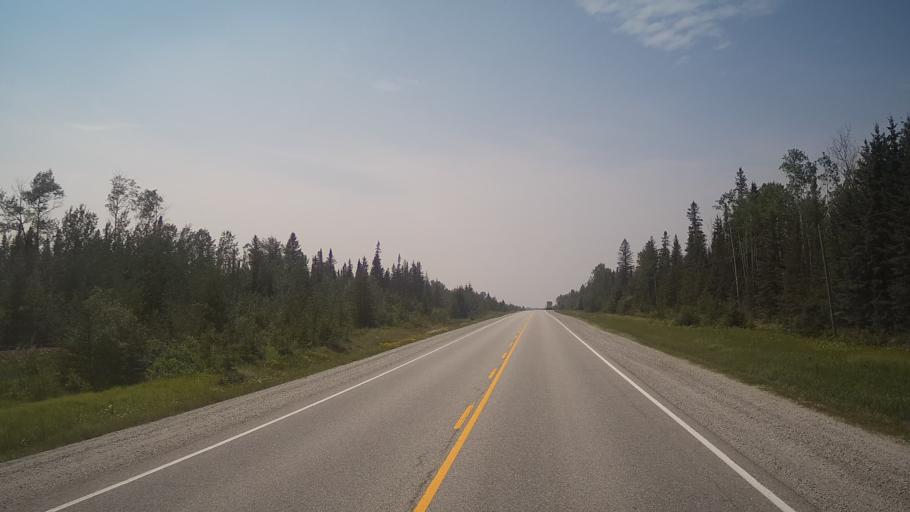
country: CA
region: Ontario
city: Kapuskasing
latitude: 49.2786
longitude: -81.7420
